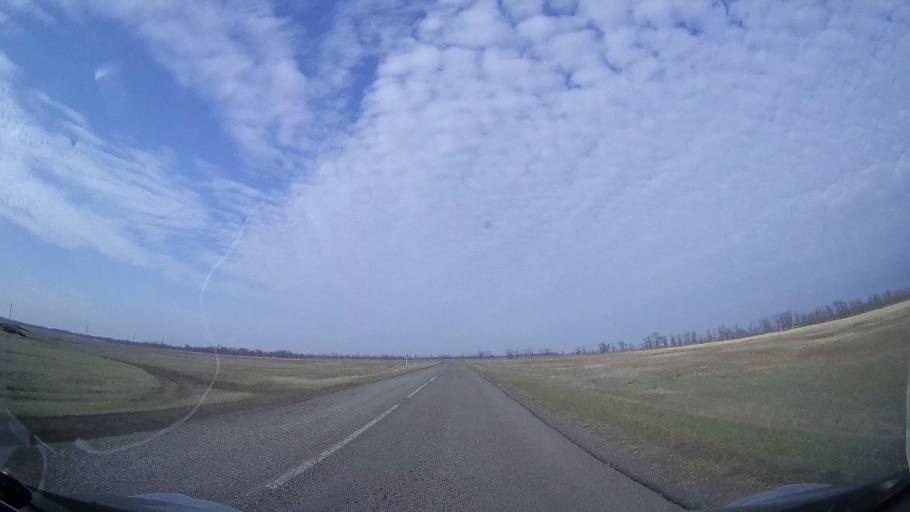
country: RU
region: Rostov
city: Gigant
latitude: 46.8491
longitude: 41.3224
